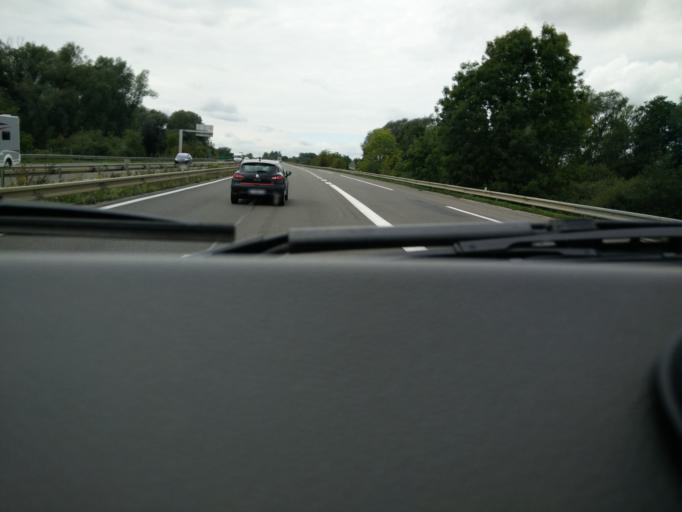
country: FR
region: Champagne-Ardenne
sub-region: Departement des Ardennes
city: Lumes
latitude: 49.7388
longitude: 4.7789
